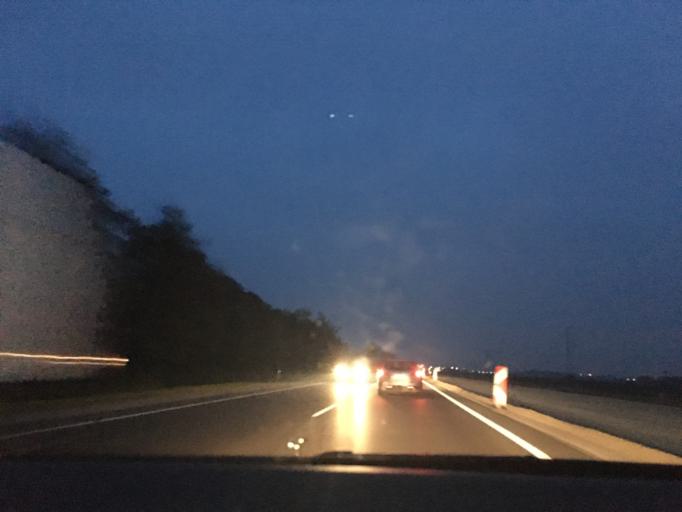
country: HU
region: Pest
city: Cegled
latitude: 47.2094
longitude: 19.7544
